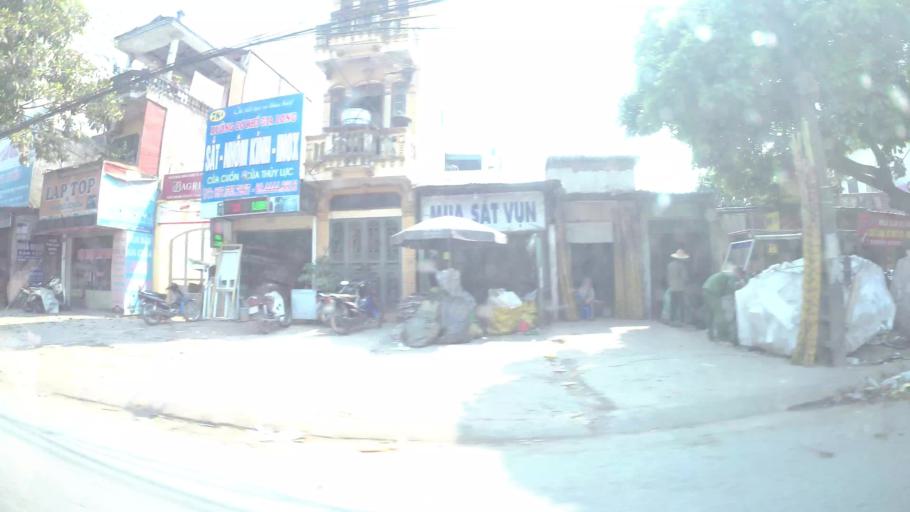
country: VN
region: Ha Noi
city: Ha Dong
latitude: 20.9581
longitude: 105.8060
